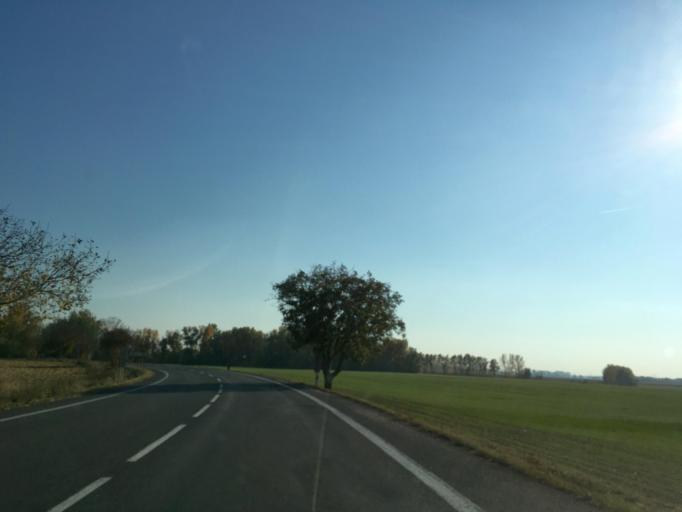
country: SK
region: Trnavsky
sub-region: Okres Dunajska Streda
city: Velky Meder
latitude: 47.8251
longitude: 17.8298
